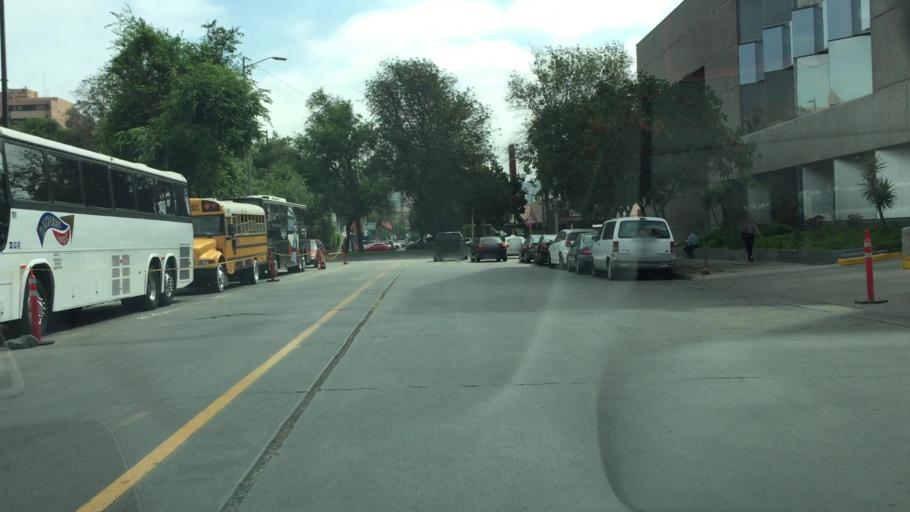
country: MX
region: Baja California
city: Tijuana
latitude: 32.5306
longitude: -117.0243
